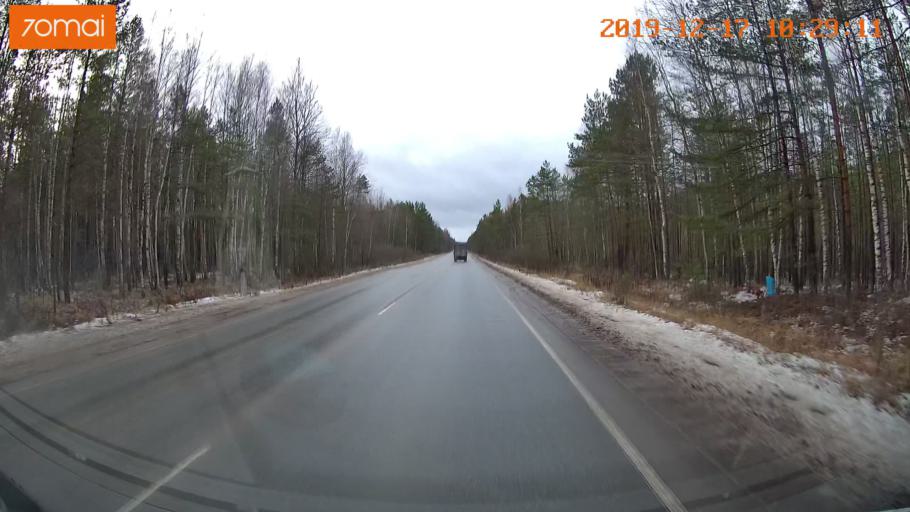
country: RU
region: Vladimir
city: Anopino
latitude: 55.6547
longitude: 40.7236
